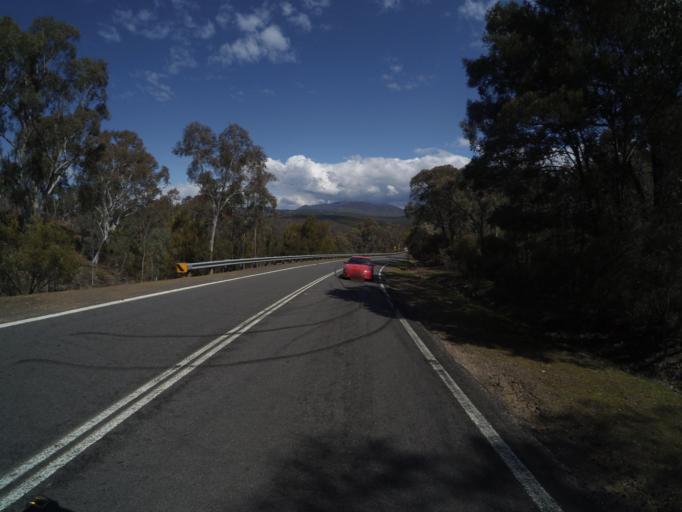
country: AU
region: Australian Capital Territory
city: Macquarie
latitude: -35.3167
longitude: 148.9485
